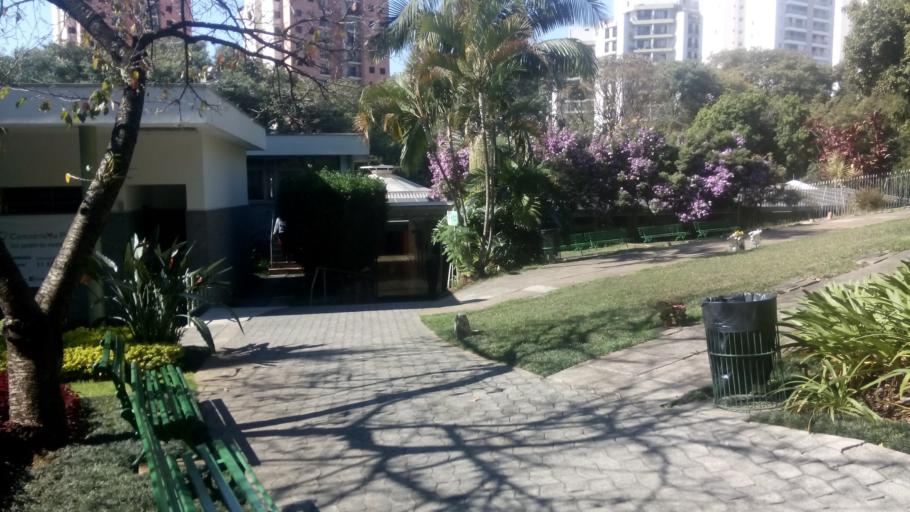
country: BR
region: Sao Paulo
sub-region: Taboao Da Serra
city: Taboao da Serra
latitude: -23.6119
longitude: -46.7447
